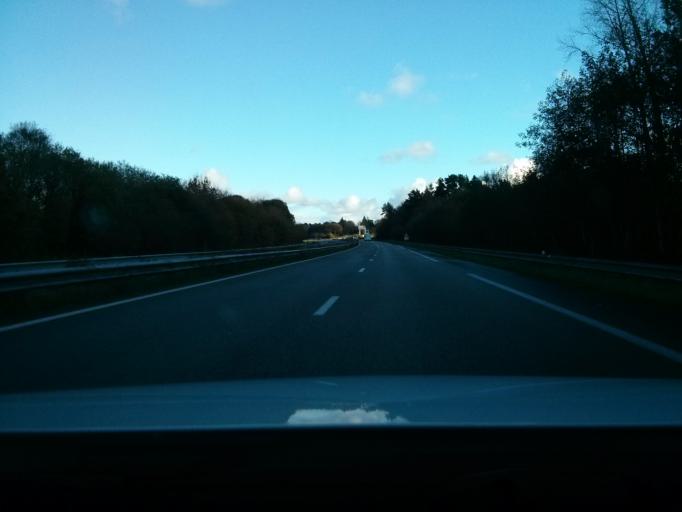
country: FR
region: Brittany
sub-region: Departement du Finistere
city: Plouigneau
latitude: 48.5763
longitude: -3.7279
